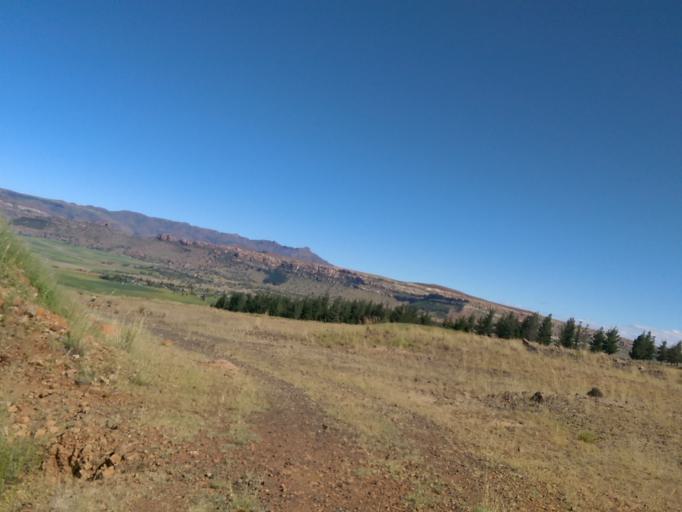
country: LS
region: Maseru
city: Maseru
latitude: -29.4866
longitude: 27.5823
